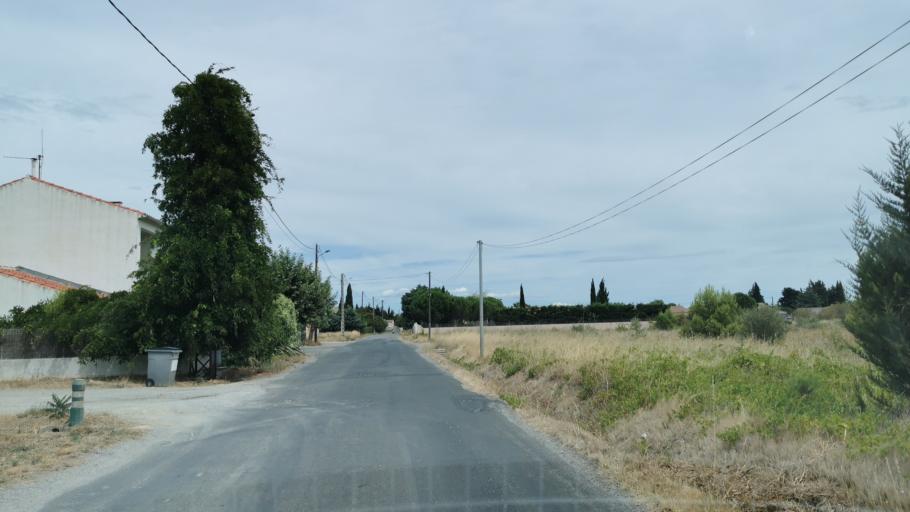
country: FR
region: Languedoc-Roussillon
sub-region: Departement de l'Aude
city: Ginestas
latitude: 43.2723
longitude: 2.8822
